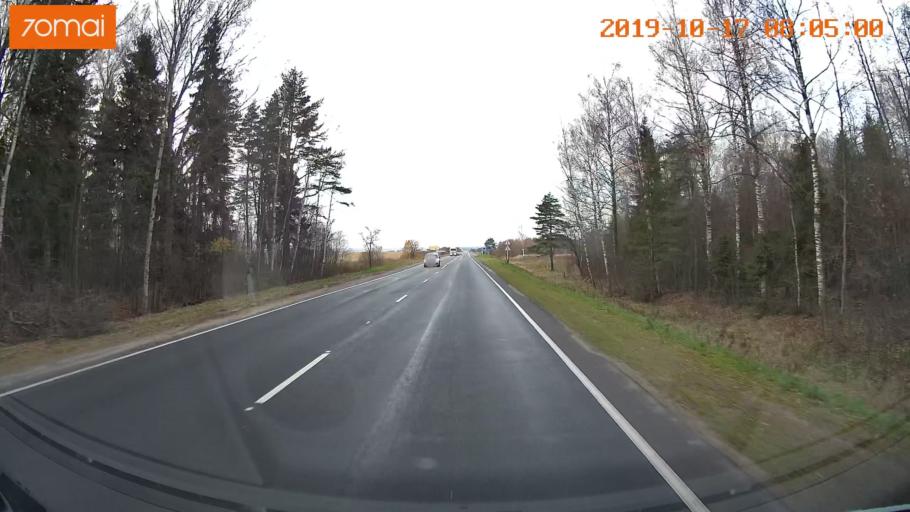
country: RU
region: Vladimir
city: Belaya Rechka
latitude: 56.3393
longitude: 39.4242
